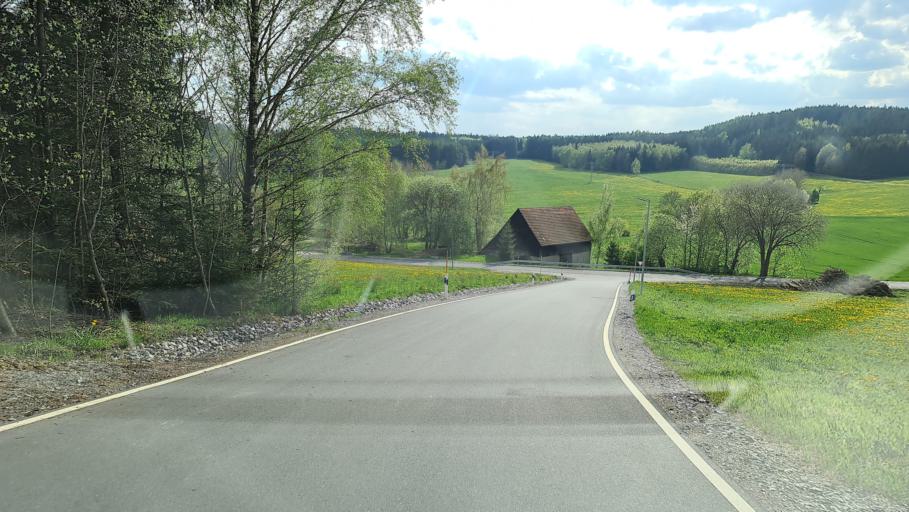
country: DE
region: Saxony
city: Schwarzenberg
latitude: 50.5184
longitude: 12.7659
